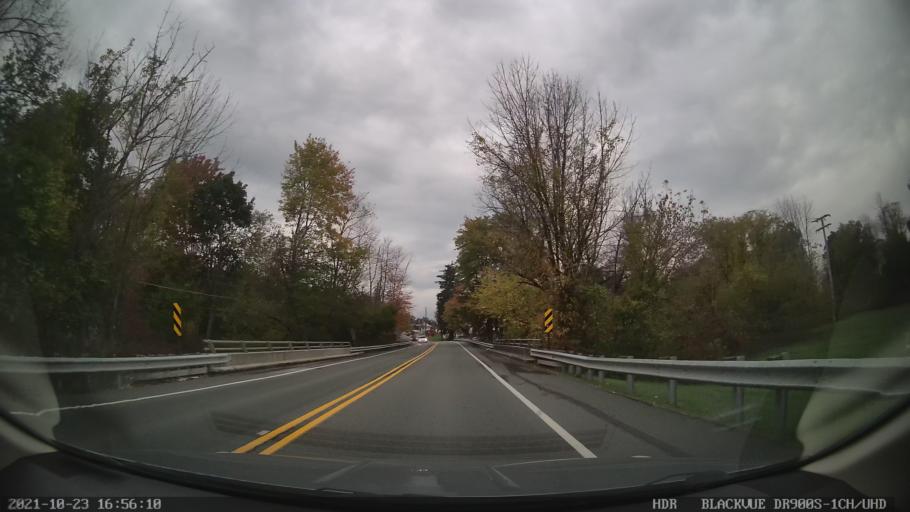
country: US
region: Pennsylvania
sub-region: Berks County
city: Bally
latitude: 40.4502
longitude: -75.5551
